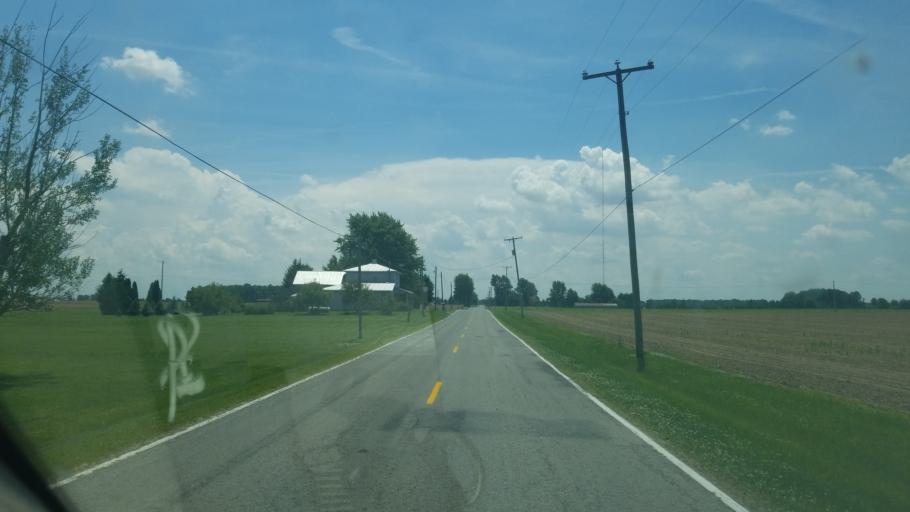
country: US
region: Ohio
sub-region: Hancock County
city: Arlington
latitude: 40.9225
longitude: -83.5946
